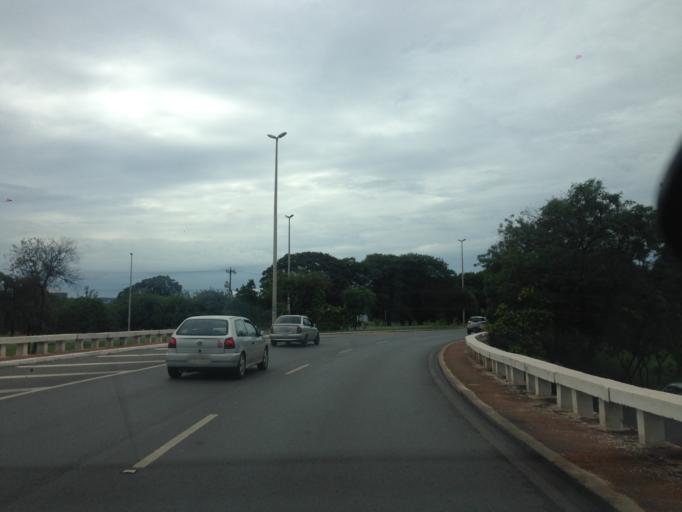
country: BR
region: Federal District
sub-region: Brasilia
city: Brasilia
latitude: -15.8022
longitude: -47.8780
